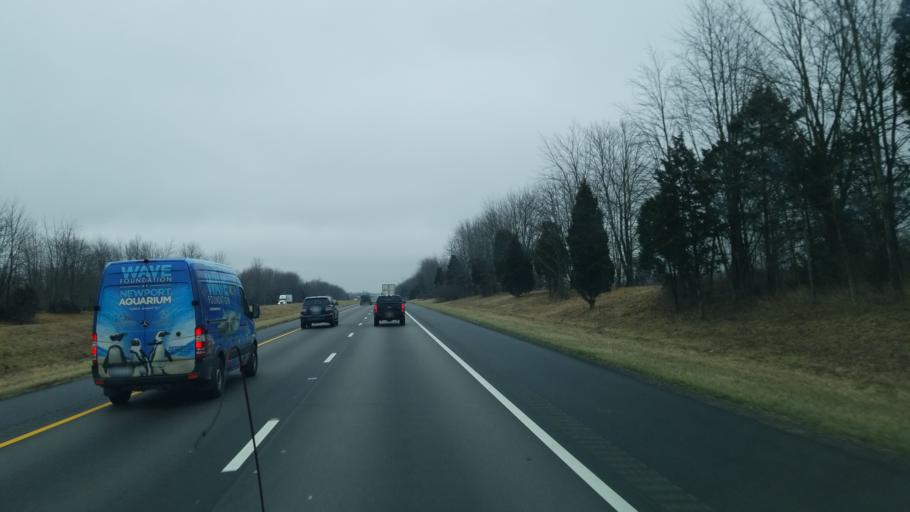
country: US
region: Ohio
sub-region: Warren County
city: Waynesville
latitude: 39.4422
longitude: -84.0443
